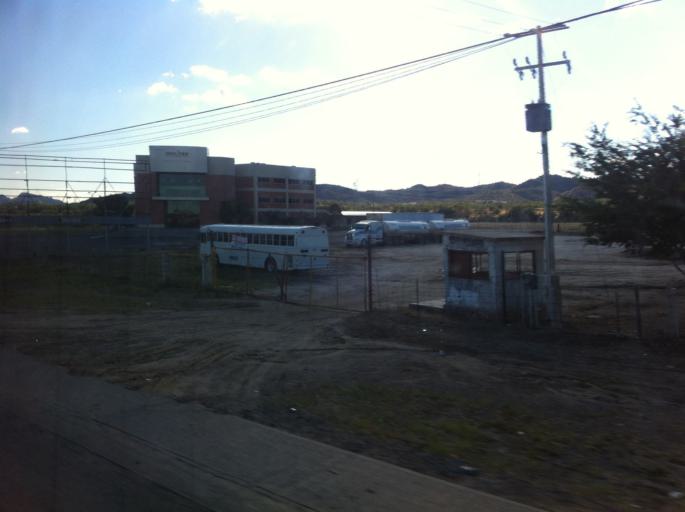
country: MX
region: Sonora
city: Hermosillo
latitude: 29.1287
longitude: -110.9125
